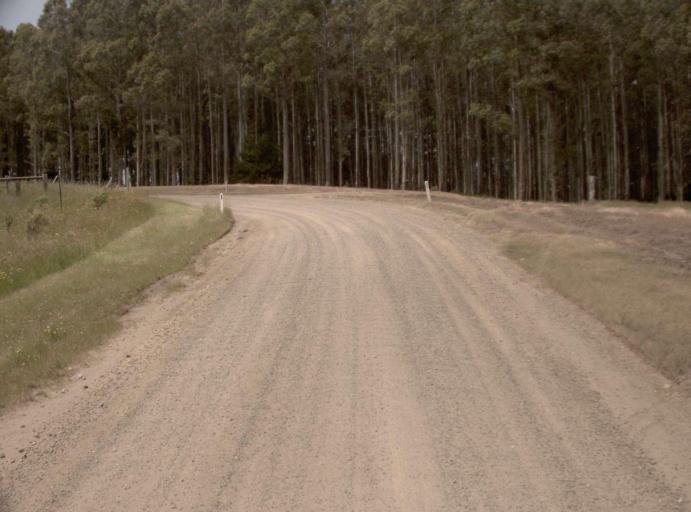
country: AU
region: Victoria
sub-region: Latrobe
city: Traralgon
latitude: -38.3775
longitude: 146.6750
